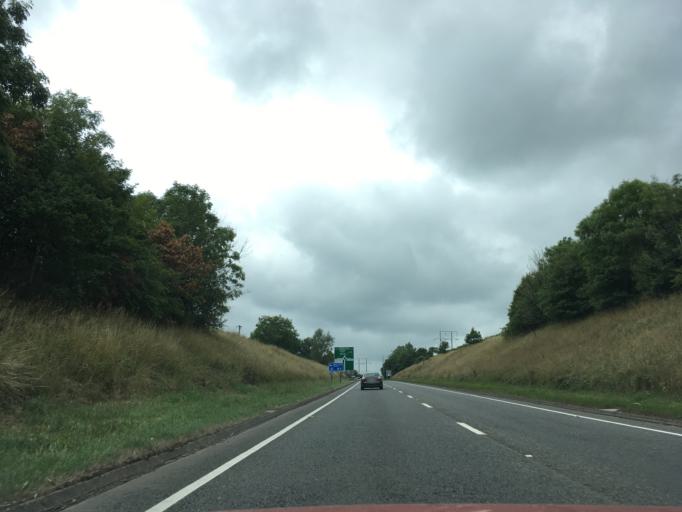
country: GB
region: Wales
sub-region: Carmarthenshire
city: Whitland
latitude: 51.8245
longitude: -4.5893
